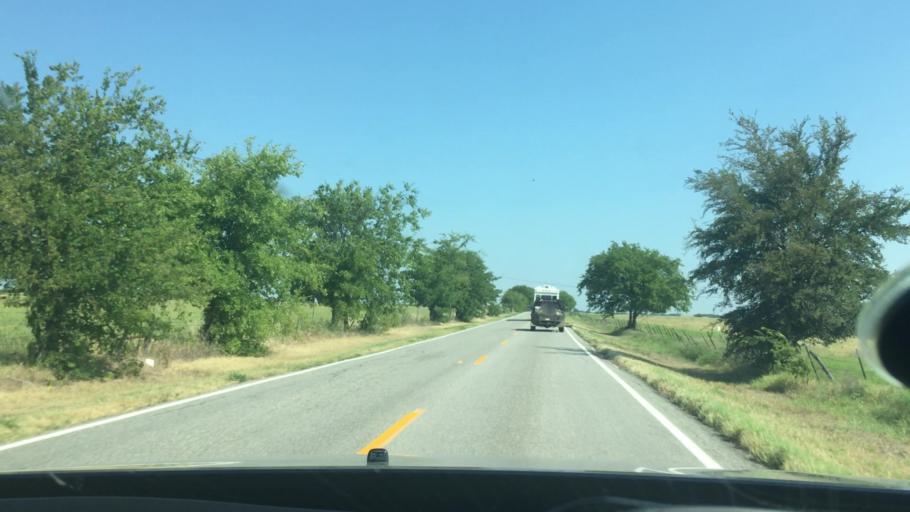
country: US
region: Oklahoma
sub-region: Johnston County
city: Tishomingo
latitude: 34.1611
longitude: -96.5078
